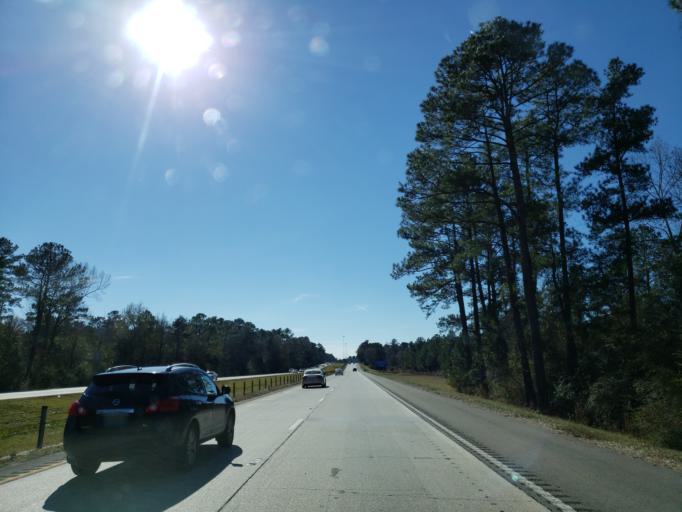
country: US
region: Mississippi
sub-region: Forrest County
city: Glendale
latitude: 31.3647
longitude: -89.3395
